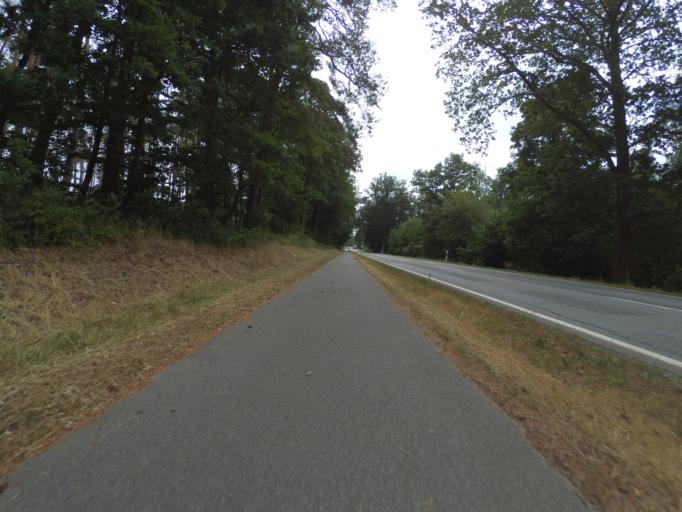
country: DE
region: Mecklenburg-Vorpommern
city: Krakow am See
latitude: 53.6210
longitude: 12.3391
